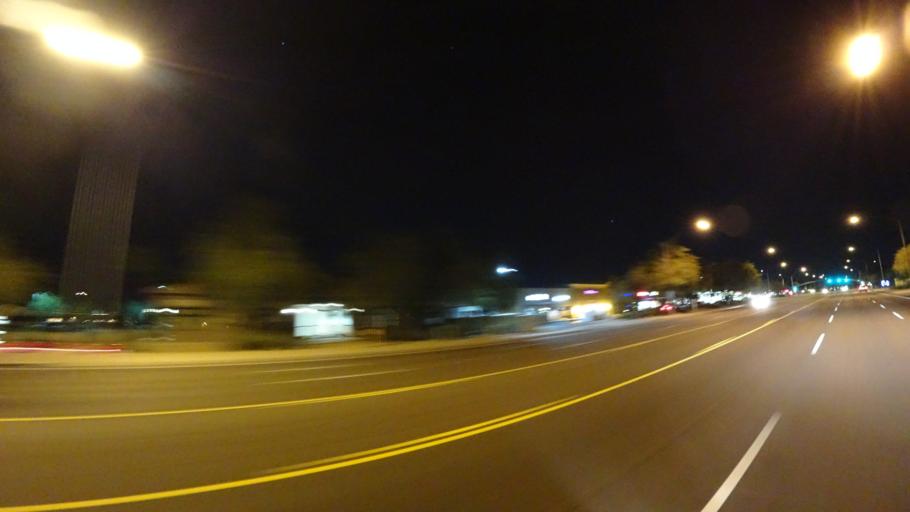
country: US
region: Arizona
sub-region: Maricopa County
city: Mesa
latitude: 33.4516
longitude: -111.8020
